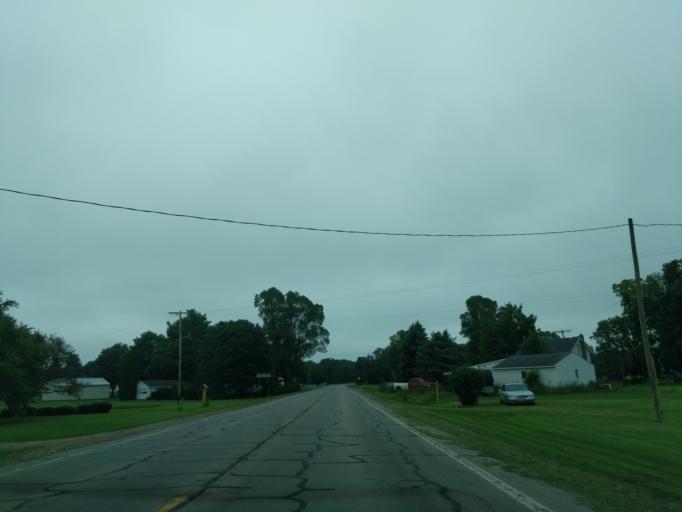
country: US
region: Michigan
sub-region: Hillsdale County
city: Litchfield
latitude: 42.0592
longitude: -84.7776
